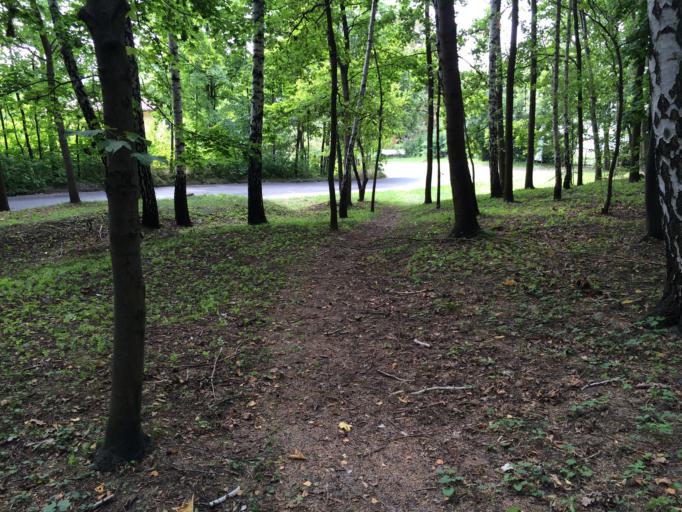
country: PL
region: Swietokrzyskie
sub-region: Powiat starachowicki
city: Starachowice
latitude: 51.0516
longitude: 21.0667
